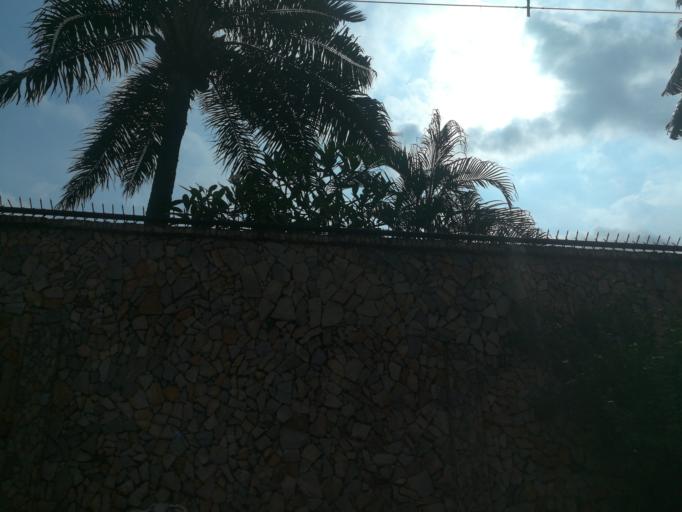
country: NG
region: Lagos
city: Oshodi
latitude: 6.5746
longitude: 3.3563
